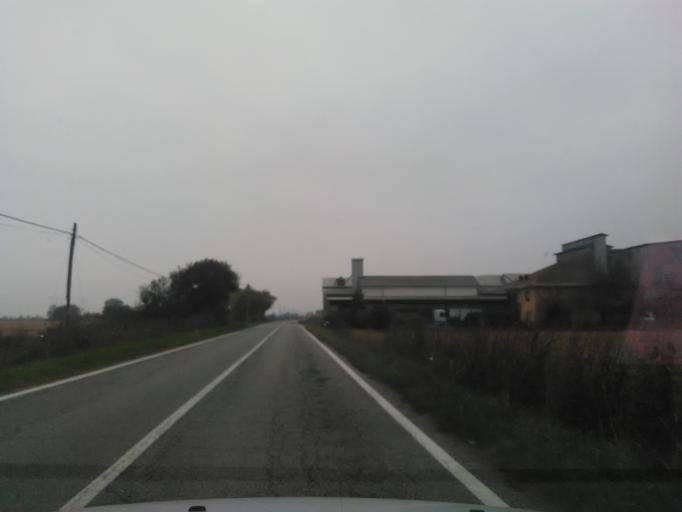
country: IT
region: Piedmont
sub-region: Provincia di Vercelli
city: Bianze
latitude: 45.2767
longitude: 8.1172
